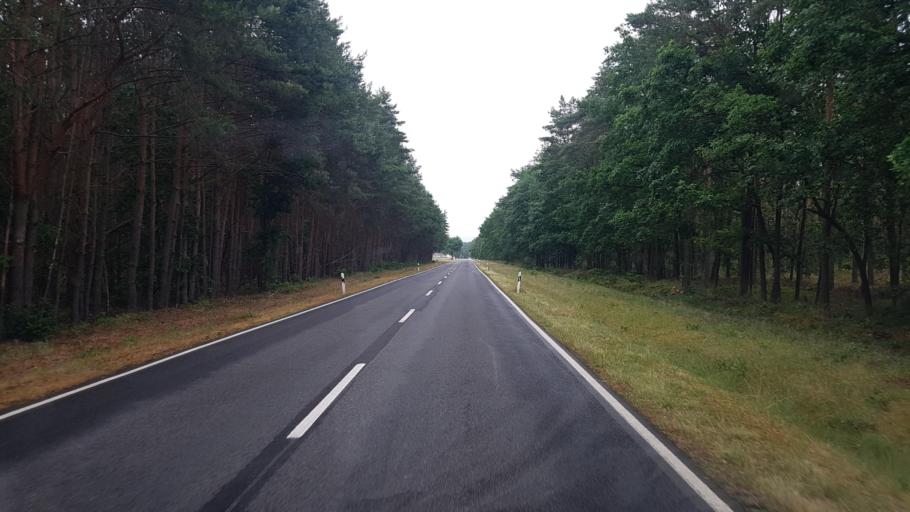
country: DE
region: Brandenburg
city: Kroppen
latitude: 51.3935
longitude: 13.8393
